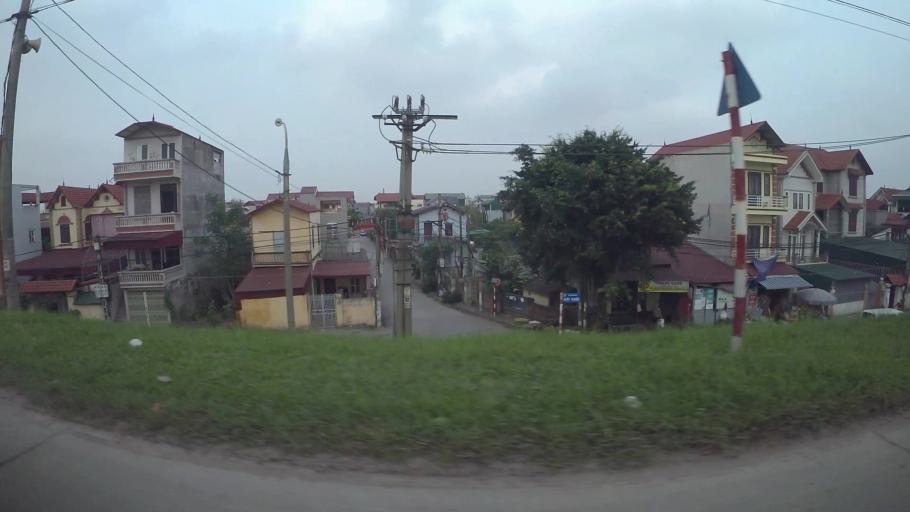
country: VN
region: Ha Noi
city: Trau Quy
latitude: 21.0070
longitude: 105.9075
